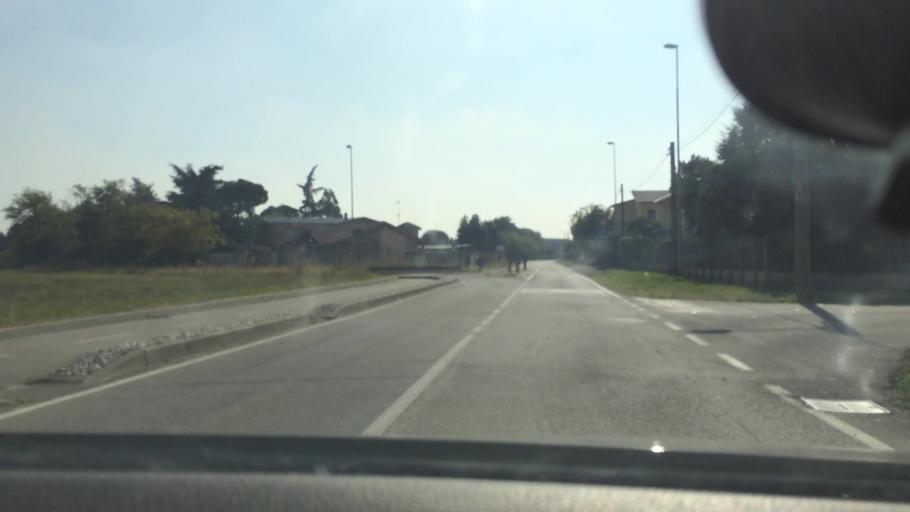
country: IT
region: Lombardy
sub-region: Citta metropolitana di Milano
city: Busto Garolfo
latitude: 45.5386
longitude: 8.8751
